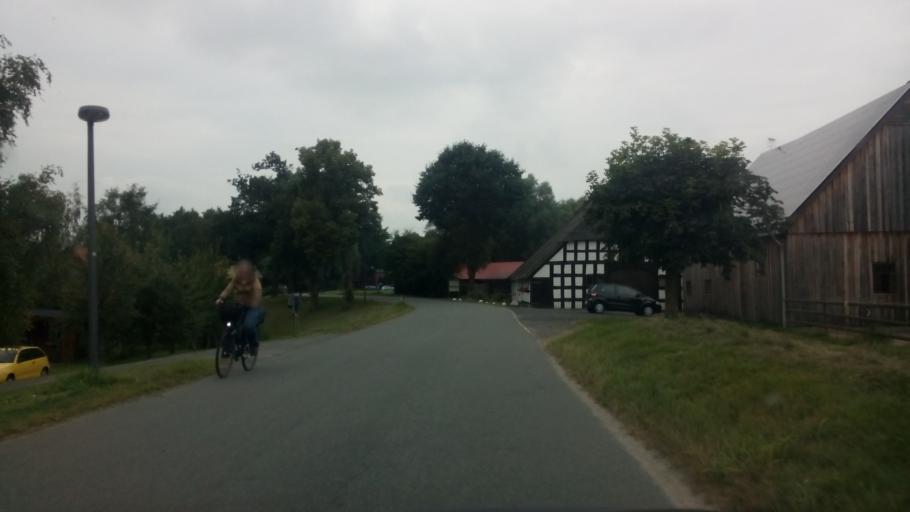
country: DE
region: Lower Saxony
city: Lilienthal
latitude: 53.1285
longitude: 8.8679
